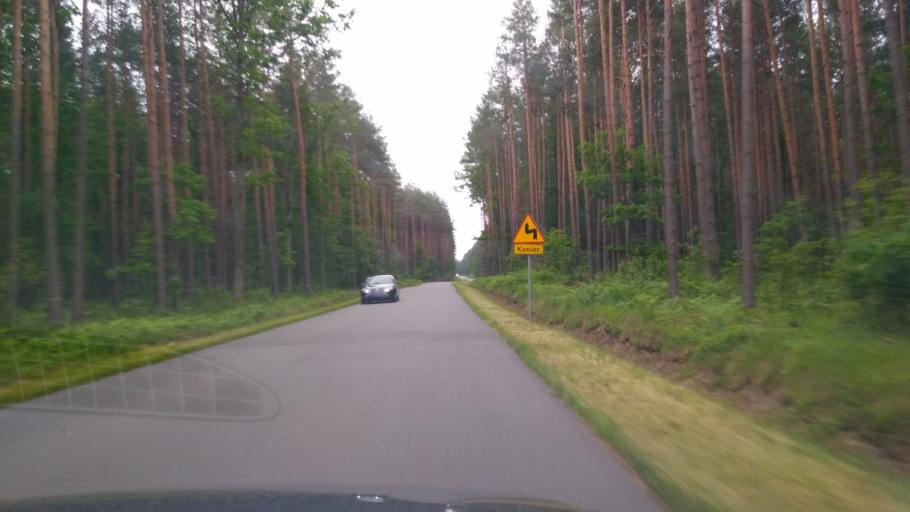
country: PL
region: Subcarpathian Voivodeship
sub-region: Powiat kolbuszowski
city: Niwiska
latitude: 50.1991
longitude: 21.6562
